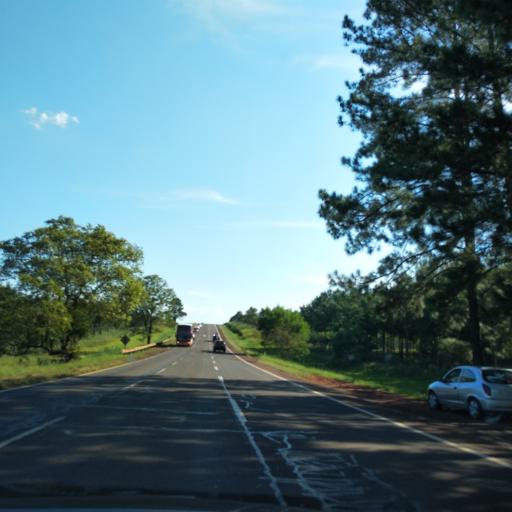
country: AR
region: Misiones
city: Santo Pipo
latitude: -27.1630
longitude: -55.4358
